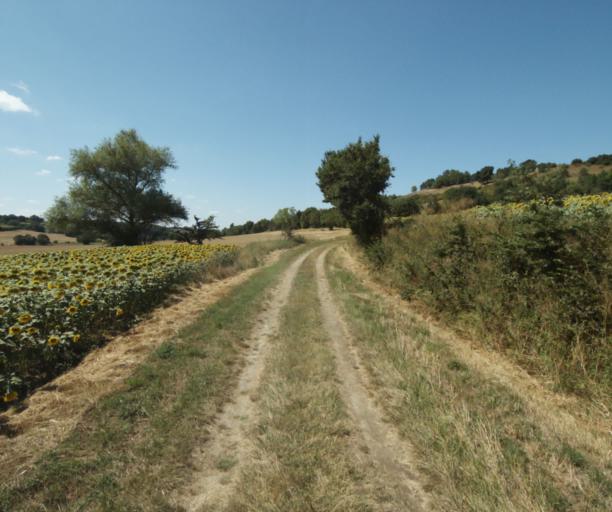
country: FR
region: Midi-Pyrenees
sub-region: Departement de la Haute-Garonne
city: Auriac-sur-Vendinelle
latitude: 43.4988
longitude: 1.8688
